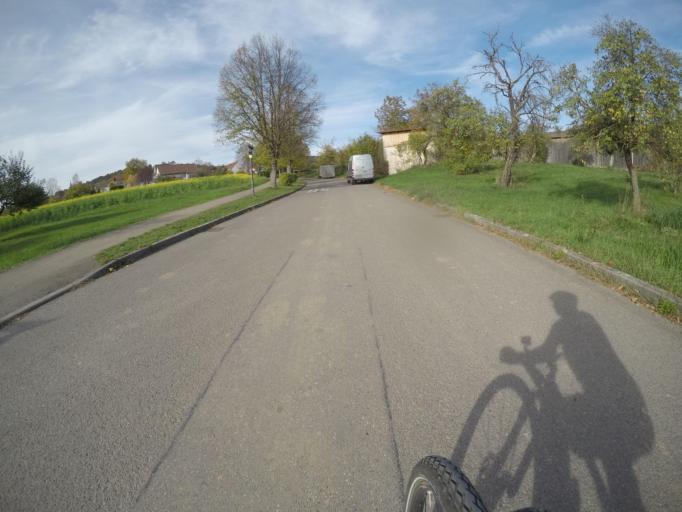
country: DE
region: Baden-Wuerttemberg
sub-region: Karlsruhe Region
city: Simmozheim
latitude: 48.7485
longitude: 8.8157
